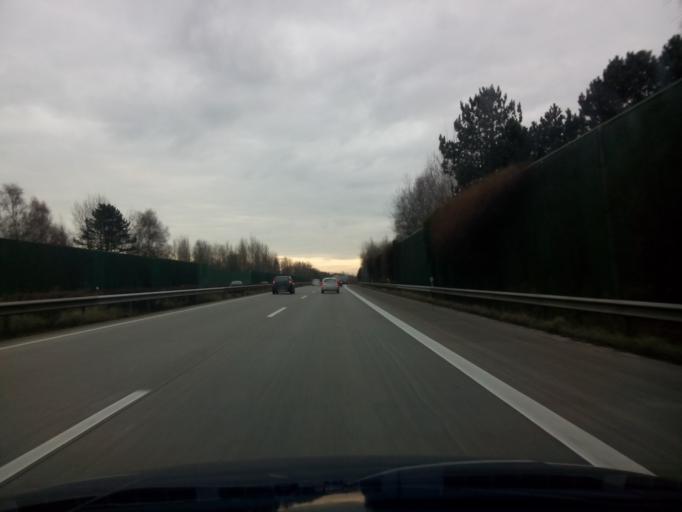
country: DE
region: Lower Saxony
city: Schiffdorf
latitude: 53.5111
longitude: 8.6288
